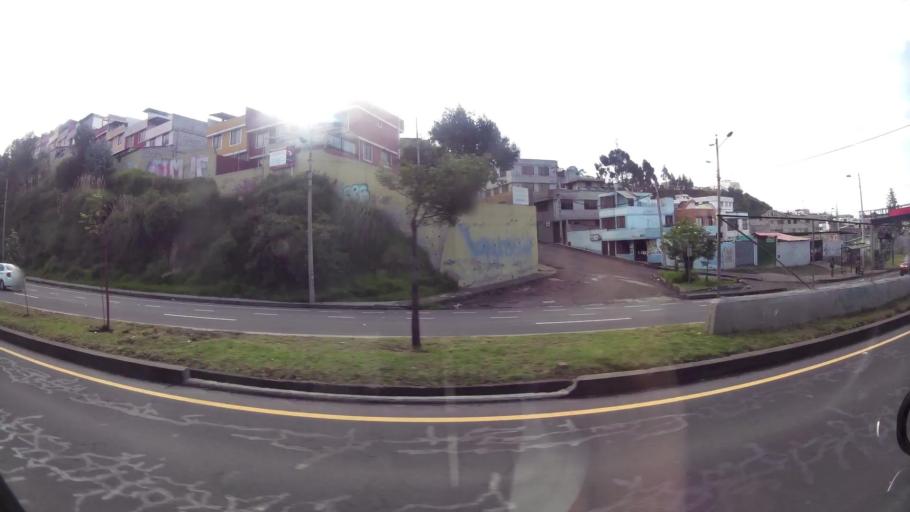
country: EC
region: Pichincha
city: Quito
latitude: -0.2376
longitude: -78.4902
